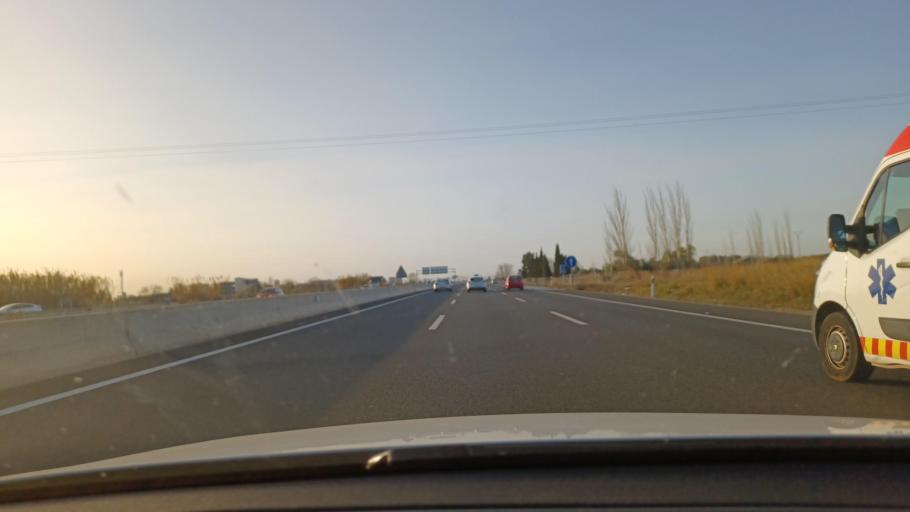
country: ES
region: Valencia
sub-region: Provincia de Valencia
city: Puig
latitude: 39.5864
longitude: -0.2939
